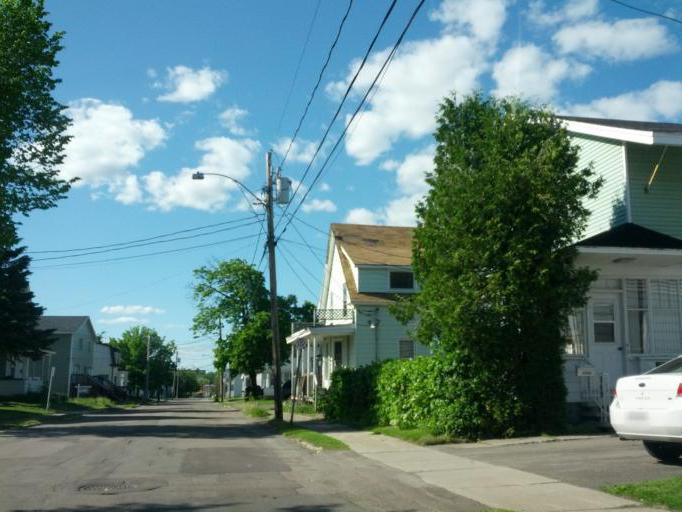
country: CA
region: New Brunswick
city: Moncton
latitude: 46.0932
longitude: -64.7765
